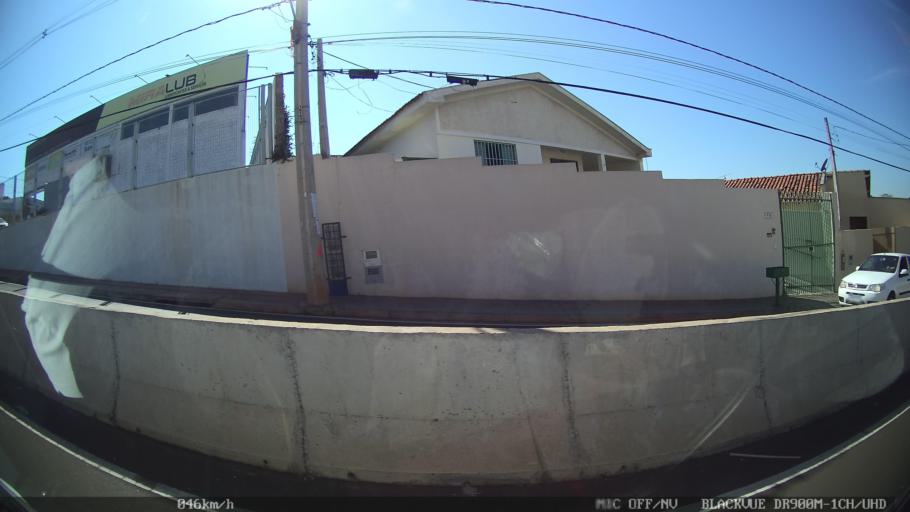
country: BR
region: Sao Paulo
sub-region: Sao Jose Do Rio Preto
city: Sao Jose do Rio Preto
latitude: -20.7882
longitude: -49.3893
